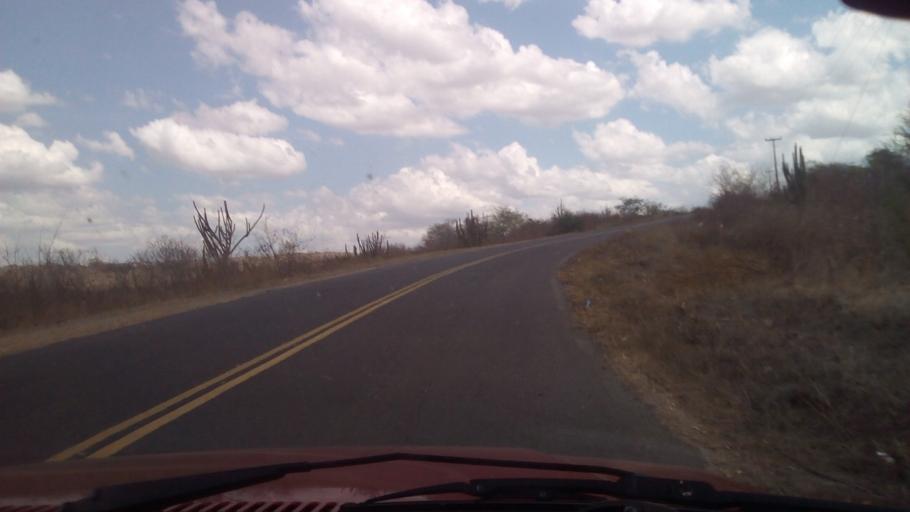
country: BR
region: Paraiba
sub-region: Cacimba De Dentro
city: Cacimba de Dentro
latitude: -6.6917
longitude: -35.7423
